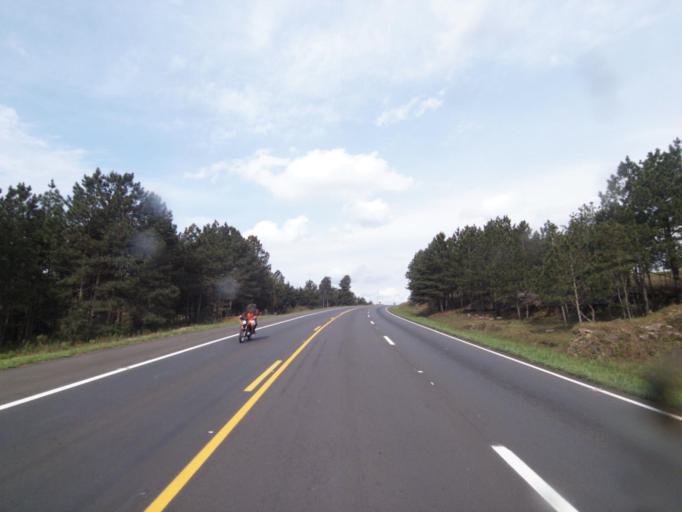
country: BR
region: Parana
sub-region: Campo Largo
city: Campo Largo
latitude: -25.4641
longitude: -49.7589
